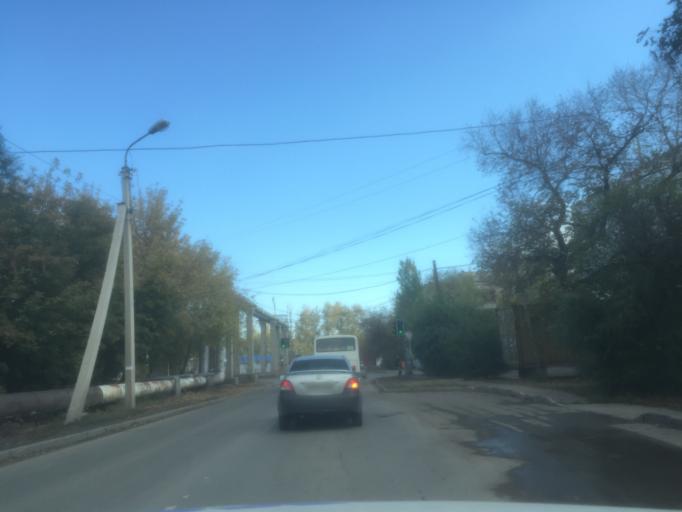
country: KZ
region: Astana Qalasy
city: Astana
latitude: 51.1941
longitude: 71.3978
